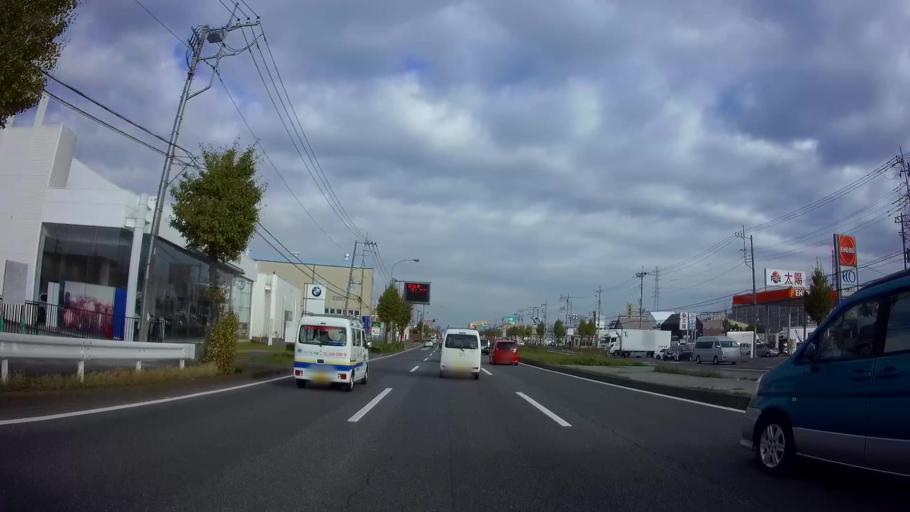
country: JP
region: Saitama
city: Yono
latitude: 35.9148
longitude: 139.5933
